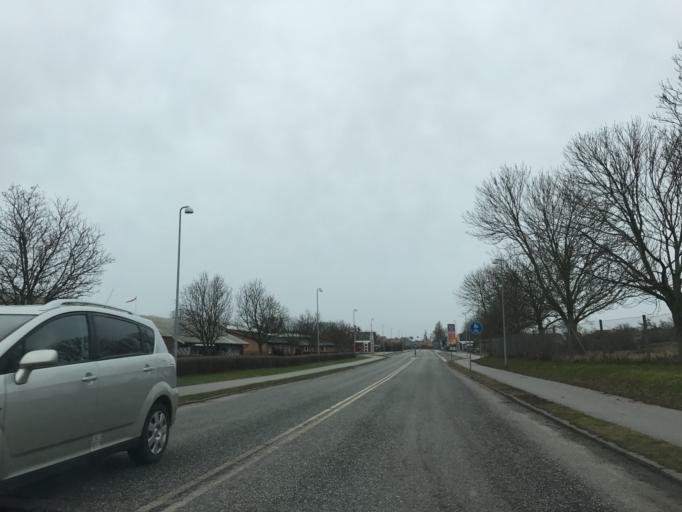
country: DK
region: South Denmark
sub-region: Langeland Kommune
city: Rudkobing
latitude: 54.9422
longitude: 10.7214
